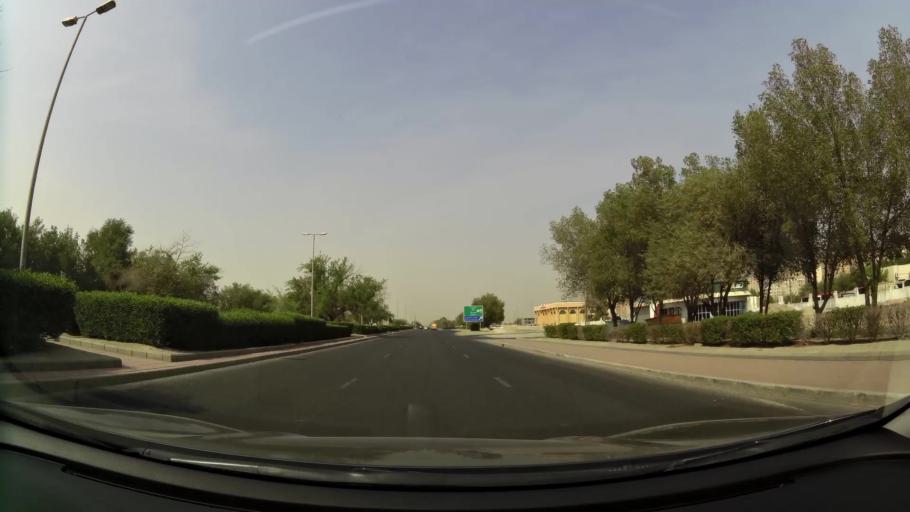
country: KW
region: Al Farwaniyah
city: Al Farwaniyah
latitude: 29.2517
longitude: 47.9242
